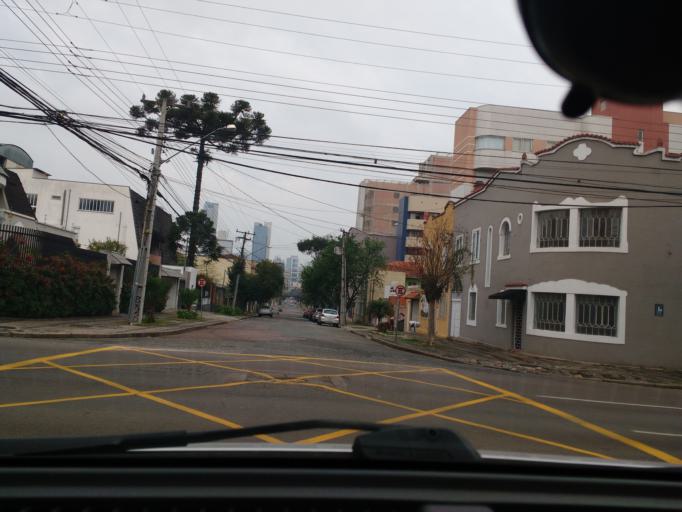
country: BR
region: Parana
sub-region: Curitiba
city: Curitiba
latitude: -25.4279
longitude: -49.2836
